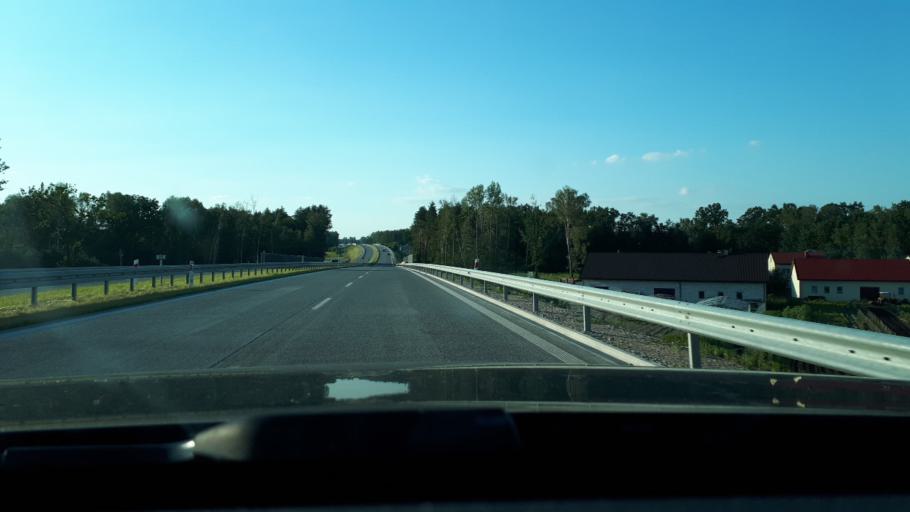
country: PL
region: Masovian Voivodeship
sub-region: Powiat piaseczynski
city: Gora Kalwaria
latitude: 51.9870
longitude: 21.1732
